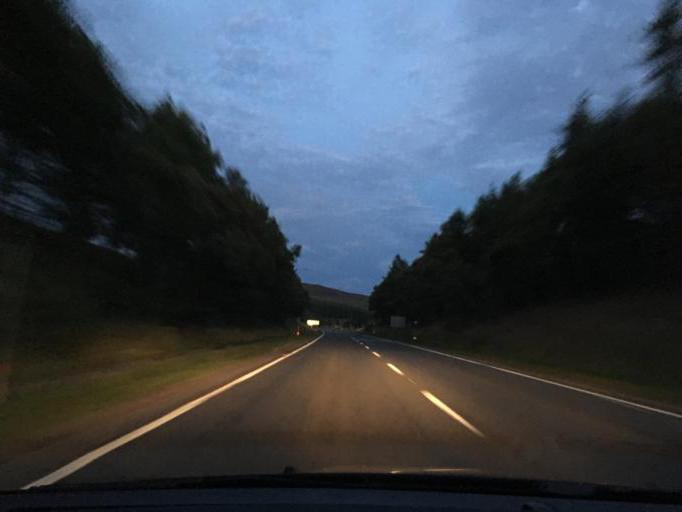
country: GB
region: Scotland
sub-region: Perth and Kinross
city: Aberfeldy
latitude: 56.8017
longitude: -4.0459
